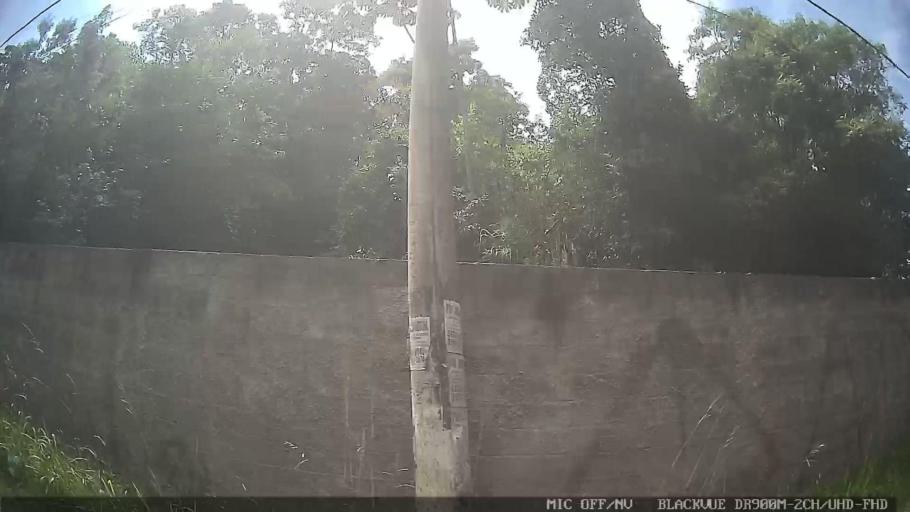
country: BR
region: Sao Paulo
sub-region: Mogi das Cruzes
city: Mogi das Cruzes
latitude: -23.4734
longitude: -46.2525
